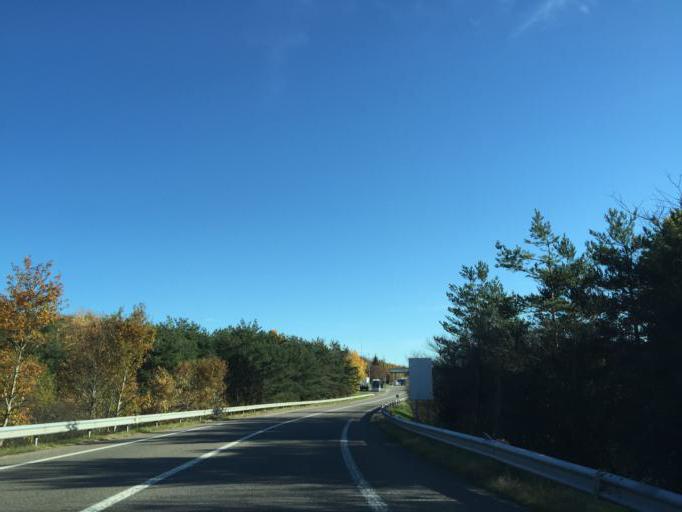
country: FR
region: Rhone-Alpes
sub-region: Departement de la Loire
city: Saint-Germain-Laval
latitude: 45.8628
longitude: 4.0395
